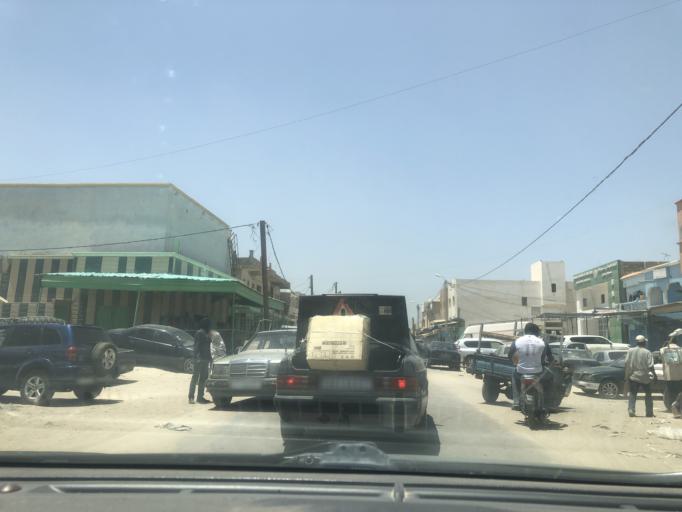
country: MR
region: Nouakchott
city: Nouakchott
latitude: 18.0735
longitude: -15.9862
